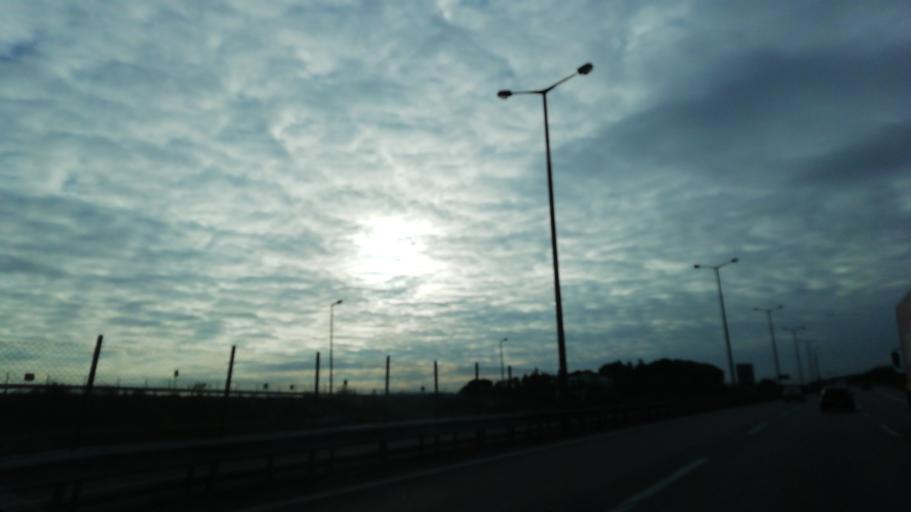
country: TR
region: Istanbul
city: Icmeler
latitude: 40.9239
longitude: 29.3506
